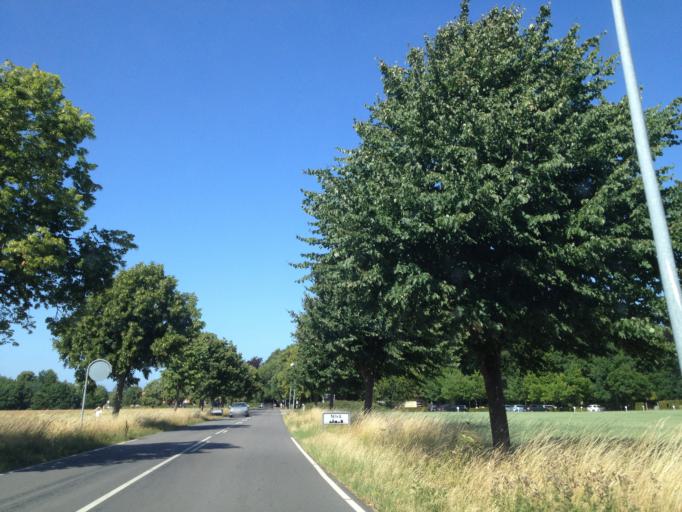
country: DK
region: Capital Region
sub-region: Fredensborg Kommune
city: Niva
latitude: 55.9256
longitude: 12.5099
